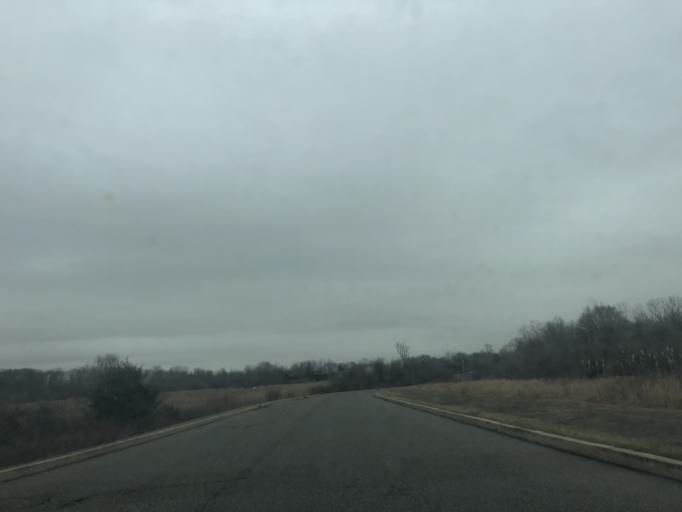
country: US
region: New Jersey
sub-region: Monmouth County
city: Allentown
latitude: 40.1870
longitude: -74.5915
